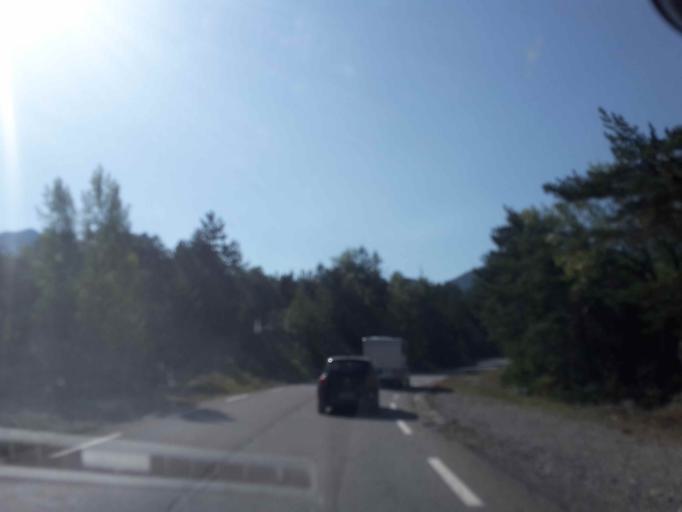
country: FR
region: Provence-Alpes-Cote d'Azur
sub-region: Departement des Hautes-Alpes
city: Guillestre
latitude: 44.6489
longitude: 6.6551
